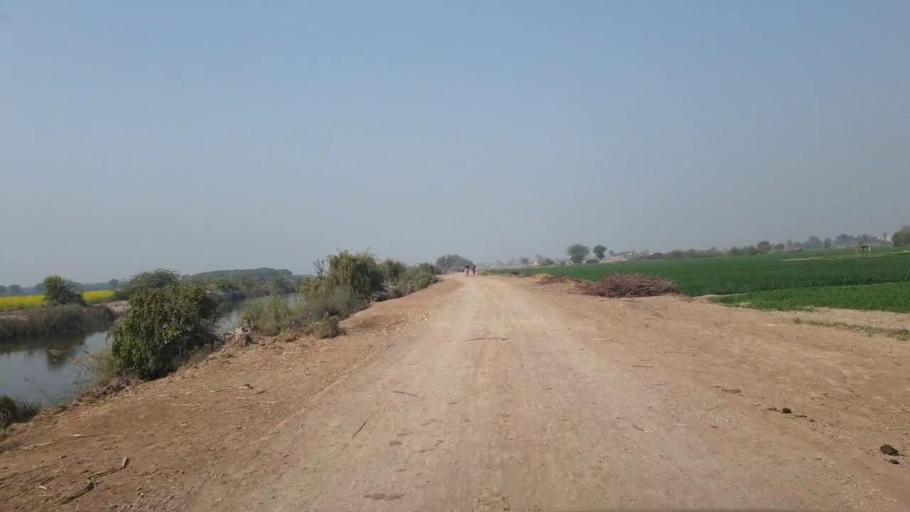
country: PK
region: Sindh
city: Hala
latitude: 25.9781
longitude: 68.4281
